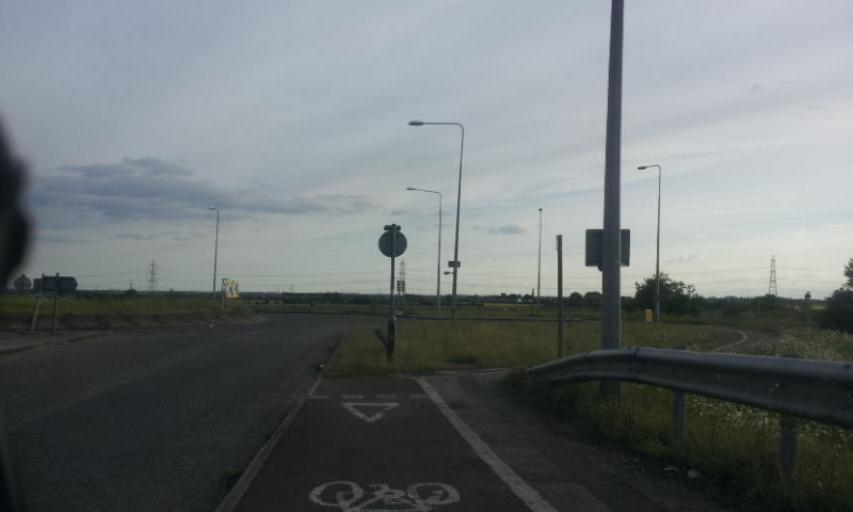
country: GB
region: England
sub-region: Kent
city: Queenborough
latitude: 51.3881
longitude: 0.7448
